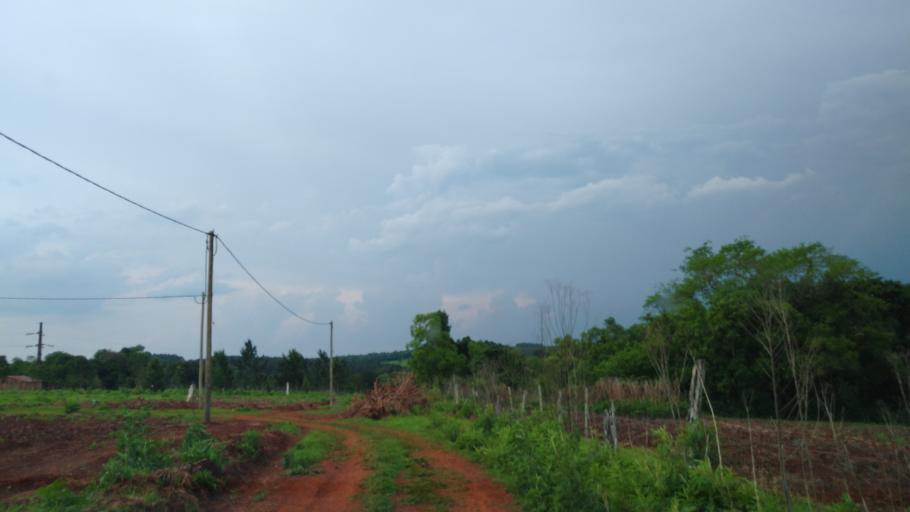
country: AR
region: Misiones
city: Capiovi
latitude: -26.9308
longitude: -55.0471
